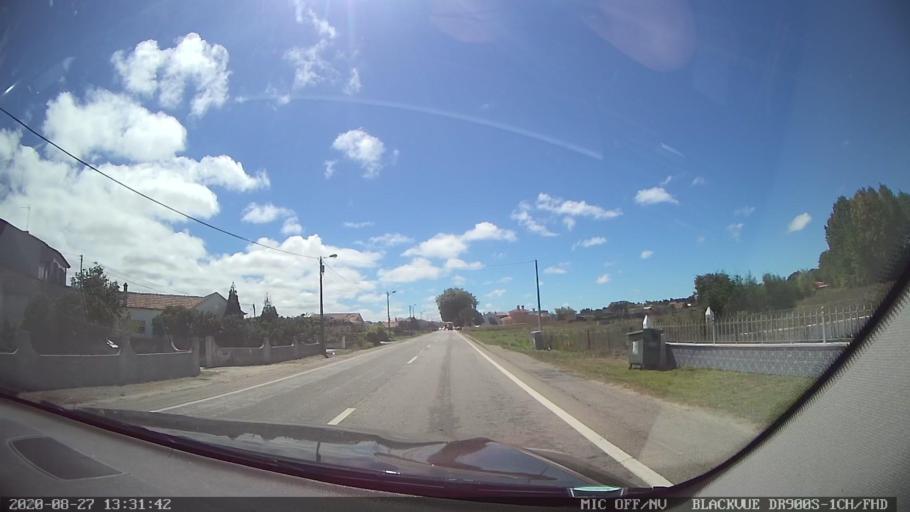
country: PT
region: Aveiro
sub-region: Vagos
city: Vagos
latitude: 40.4941
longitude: -8.6846
